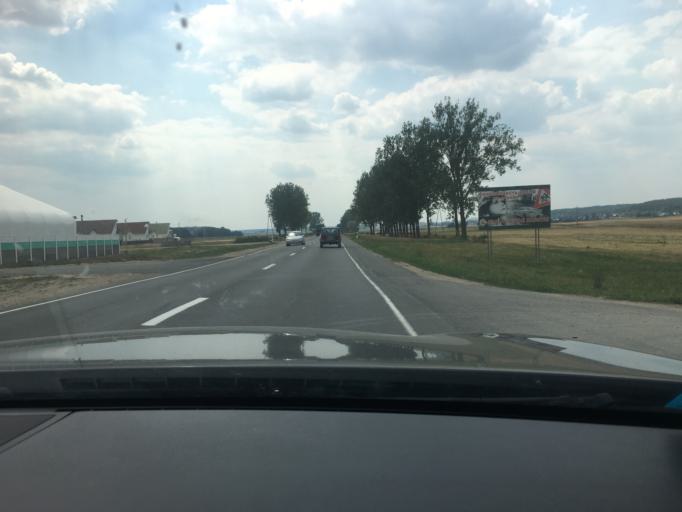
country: BY
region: Brest
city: Ruzhany
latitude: 52.8587
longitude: 24.8884
